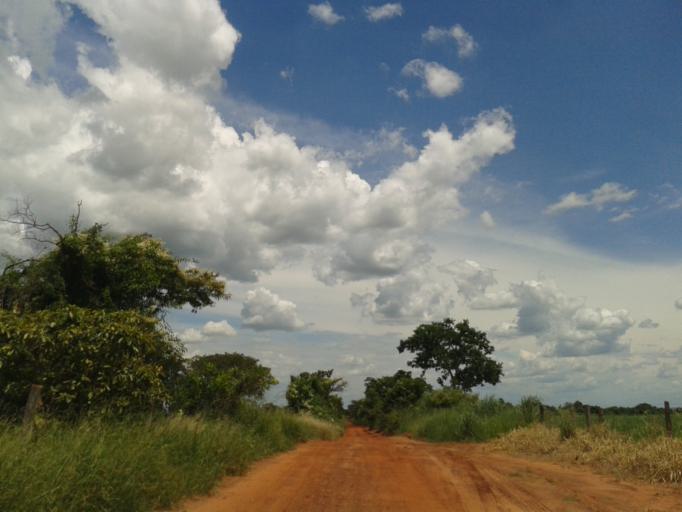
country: BR
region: Minas Gerais
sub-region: Ituiutaba
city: Ituiutaba
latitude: -18.8788
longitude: -49.4774
